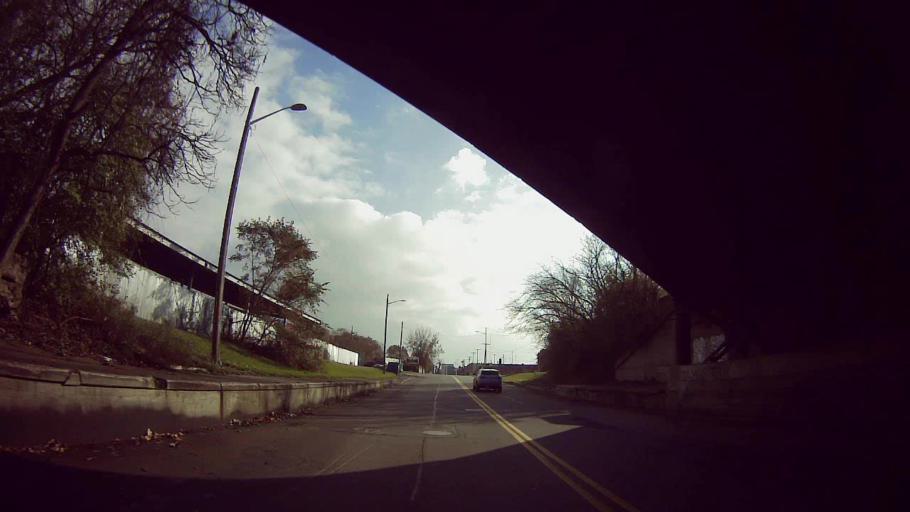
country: US
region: Michigan
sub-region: Wayne County
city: Detroit
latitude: 42.3342
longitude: -83.1003
